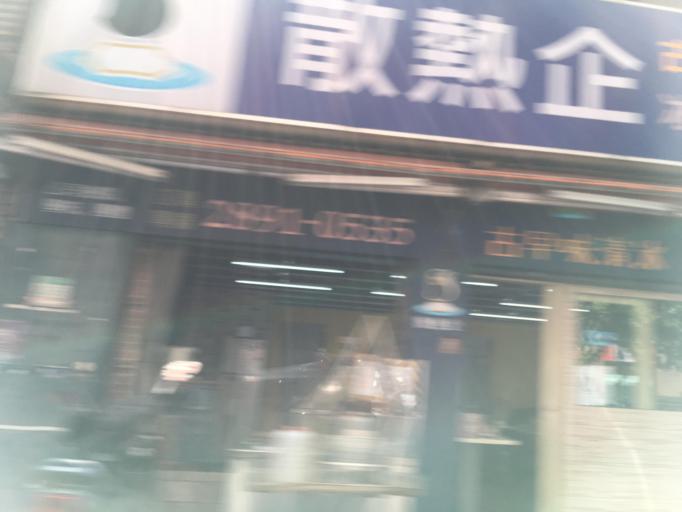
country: TW
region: Taipei
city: Taipei
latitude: 25.1417
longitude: 121.4991
